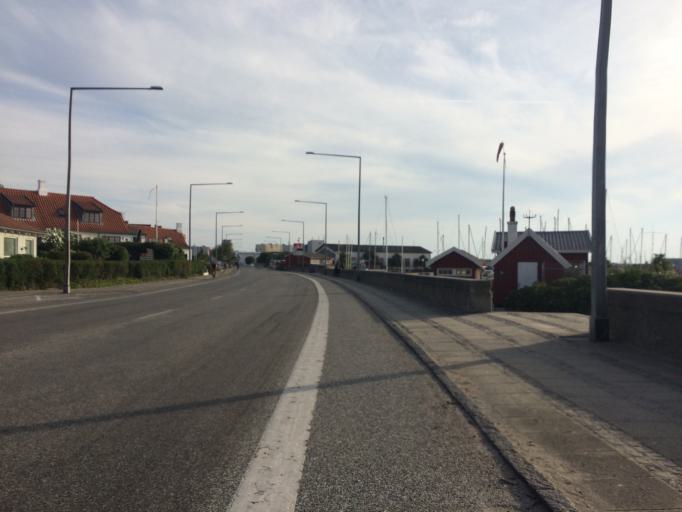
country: DK
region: Capital Region
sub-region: Bornholm Kommune
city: Ronne
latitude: 55.1040
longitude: 14.6951
